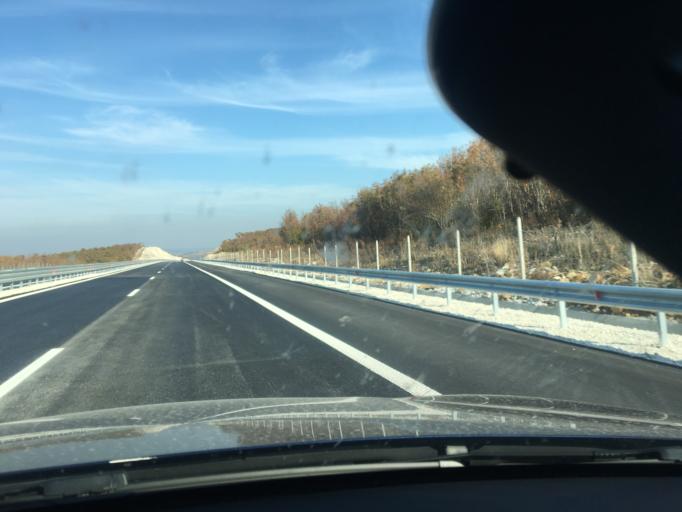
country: BG
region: Lovech
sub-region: Obshtina Yablanitsa
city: Yablanitsa
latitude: 43.0503
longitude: 24.1568
